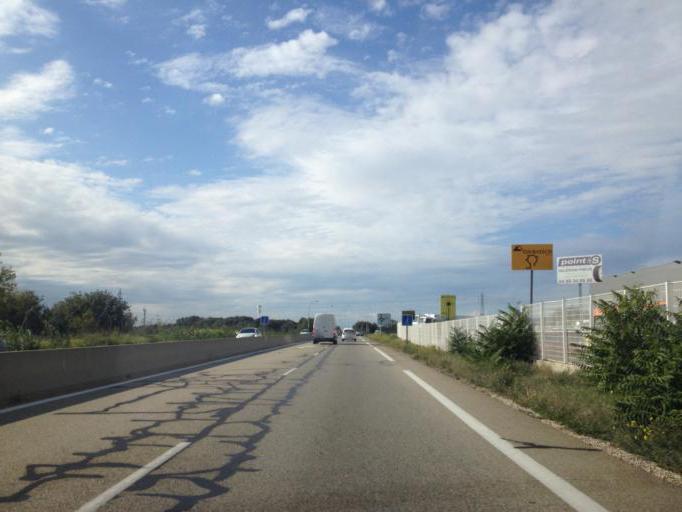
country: FR
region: Provence-Alpes-Cote d'Azur
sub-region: Departement du Vaucluse
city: Orange
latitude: 44.1160
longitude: 4.8401
